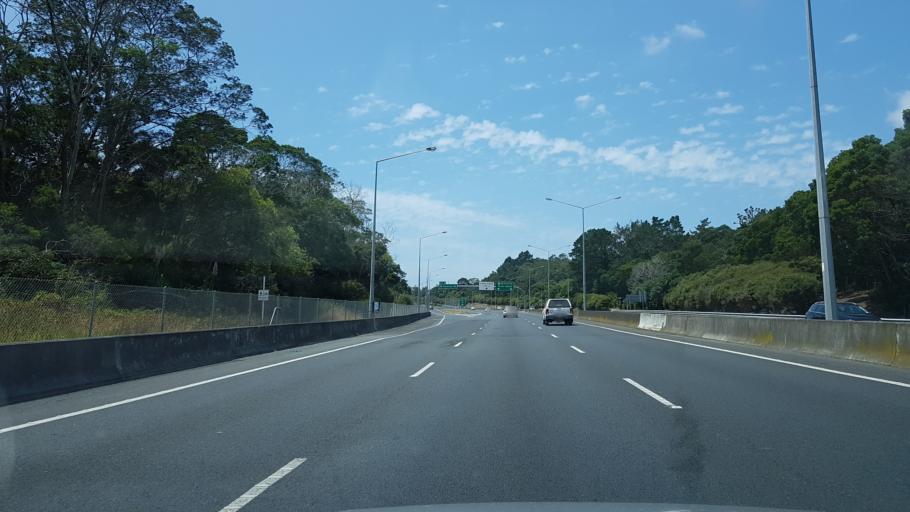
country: NZ
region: Auckland
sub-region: Auckland
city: North Shore
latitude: -36.7843
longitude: 174.6702
